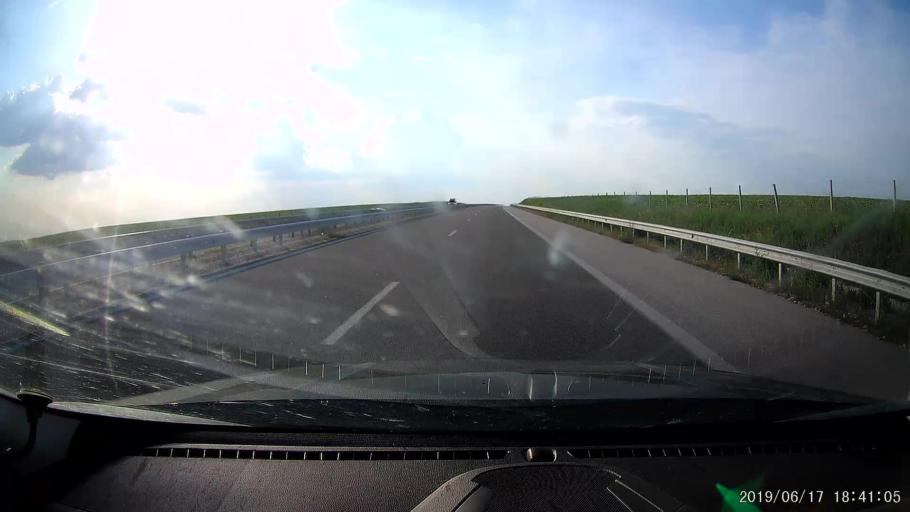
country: BG
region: Stara Zagora
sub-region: Obshtina Chirpan
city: Chirpan
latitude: 42.1654
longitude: 25.2626
